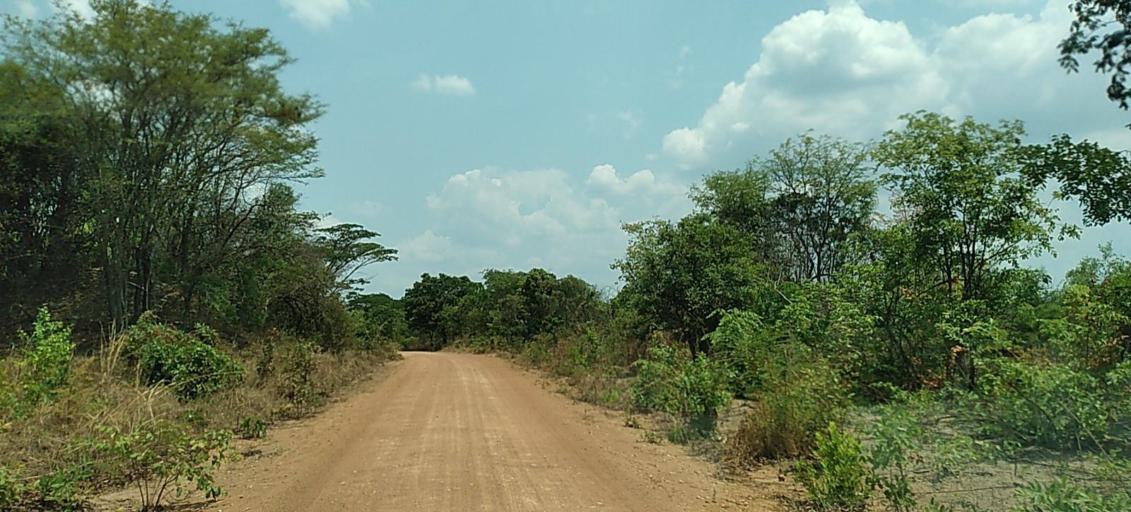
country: ZM
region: Copperbelt
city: Luanshya
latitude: -13.1390
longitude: 28.3144
